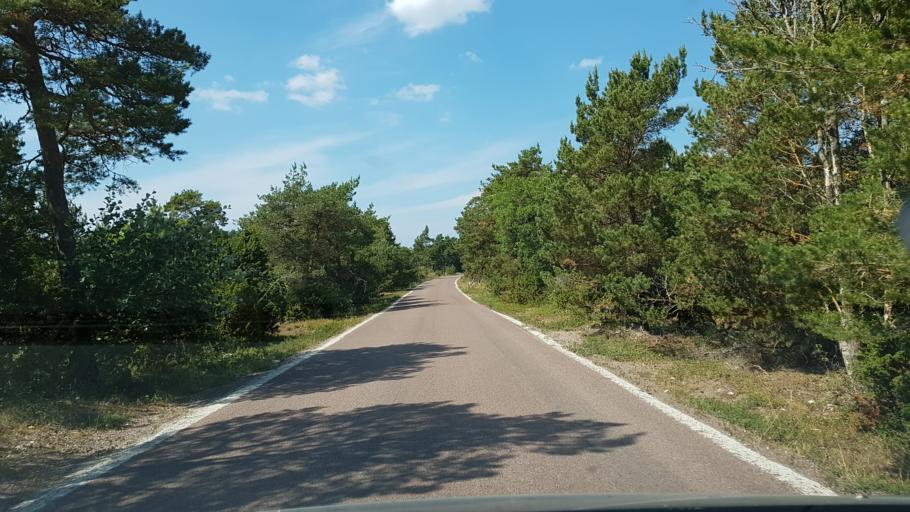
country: SE
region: Gotland
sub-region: Gotland
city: Visby
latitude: 57.6707
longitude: 18.3644
